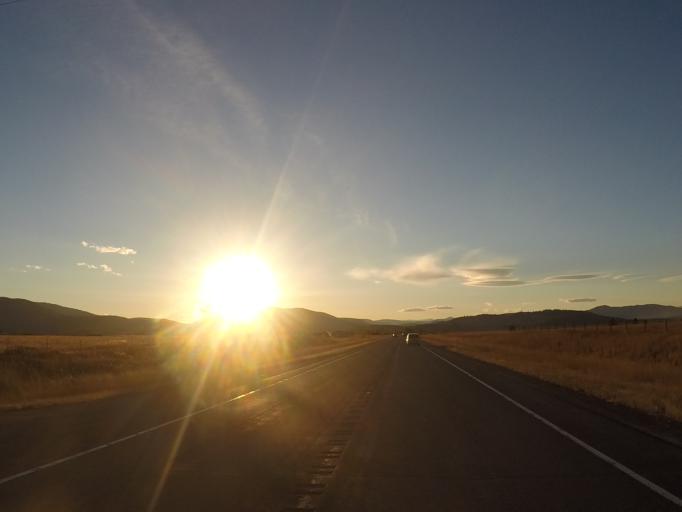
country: US
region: Montana
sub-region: Missoula County
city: Seeley Lake
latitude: 47.0201
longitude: -113.1127
